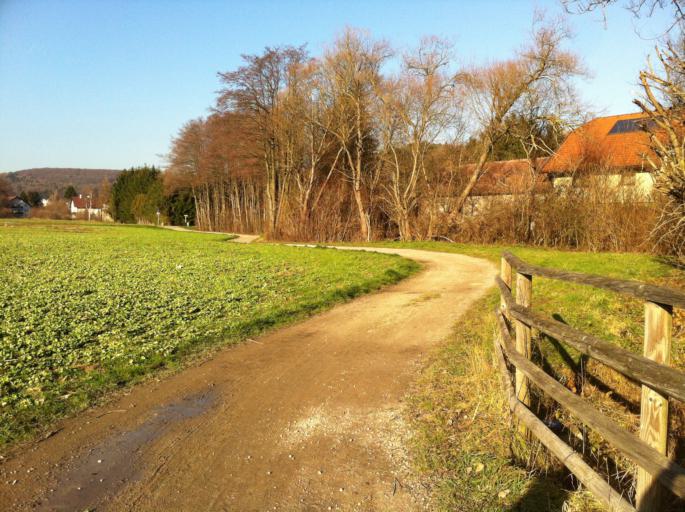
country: AT
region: Lower Austria
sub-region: Politischer Bezirk Wien-Umgebung
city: Gablitz
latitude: 48.2330
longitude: 16.1439
